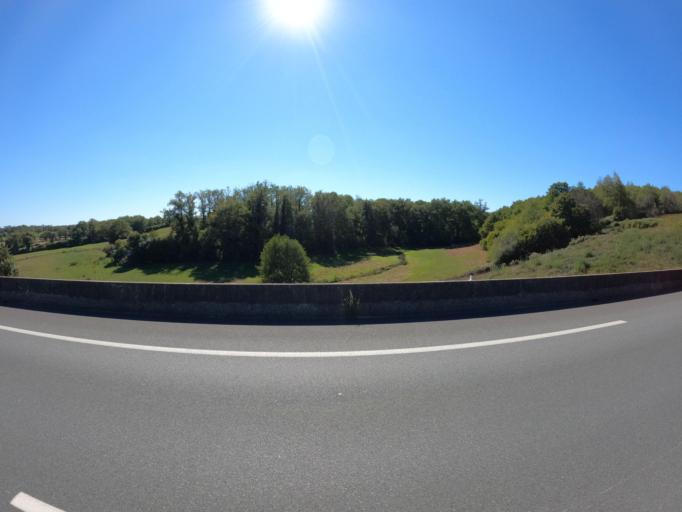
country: FR
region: Limousin
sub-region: Departement de la Creuse
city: Ajain
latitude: 46.2041
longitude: 2.0970
